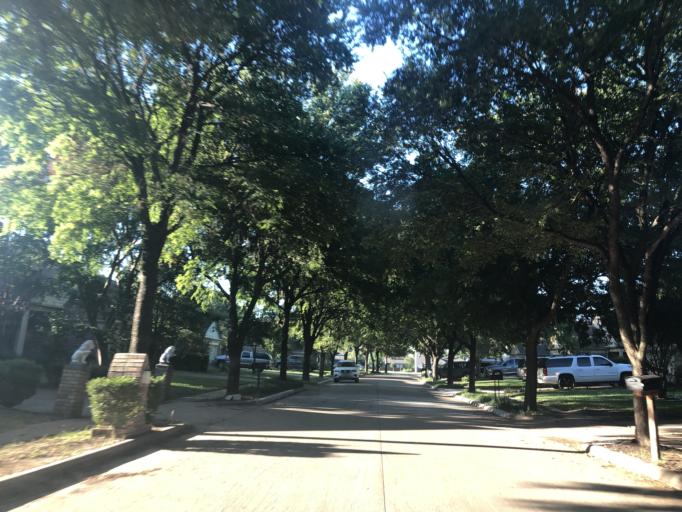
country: US
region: Texas
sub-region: Dallas County
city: Grand Prairie
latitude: 32.6651
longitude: -96.9987
